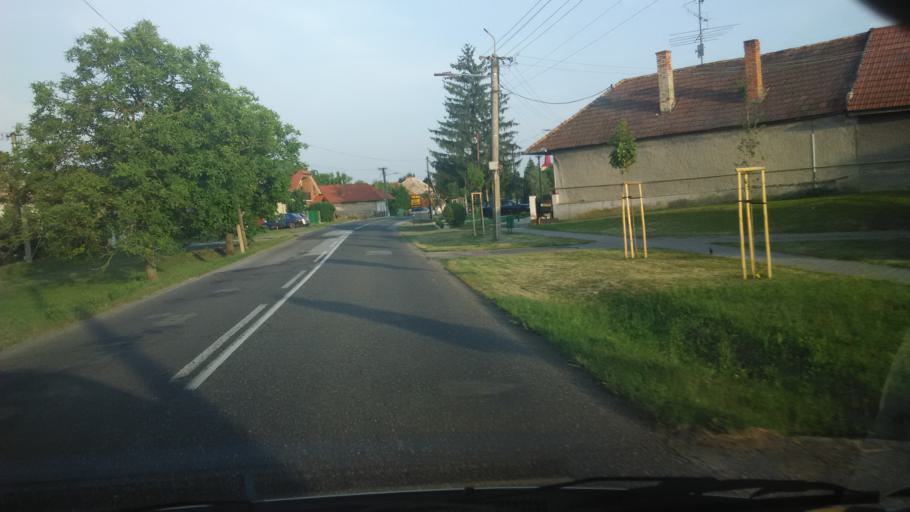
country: SK
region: Nitriansky
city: Tlmace
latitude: 48.2465
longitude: 18.5186
